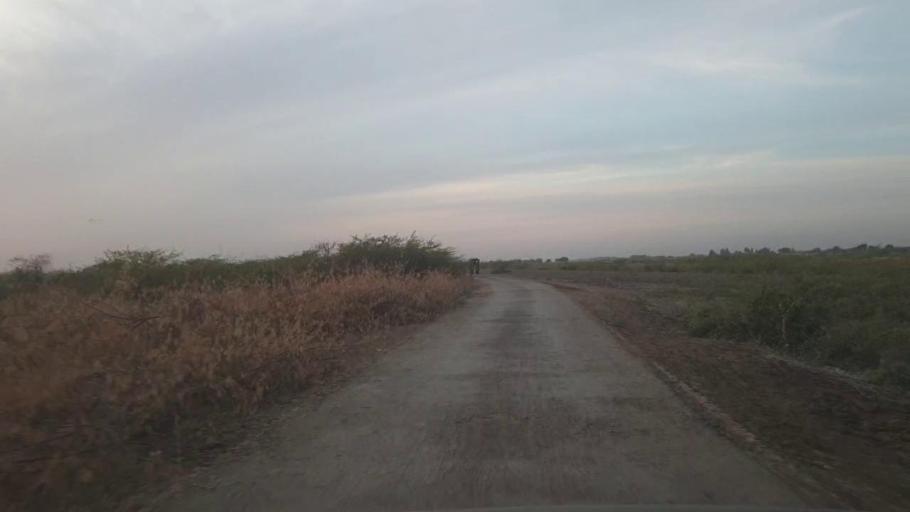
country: PK
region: Sindh
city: Kunri
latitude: 25.2316
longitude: 69.5309
